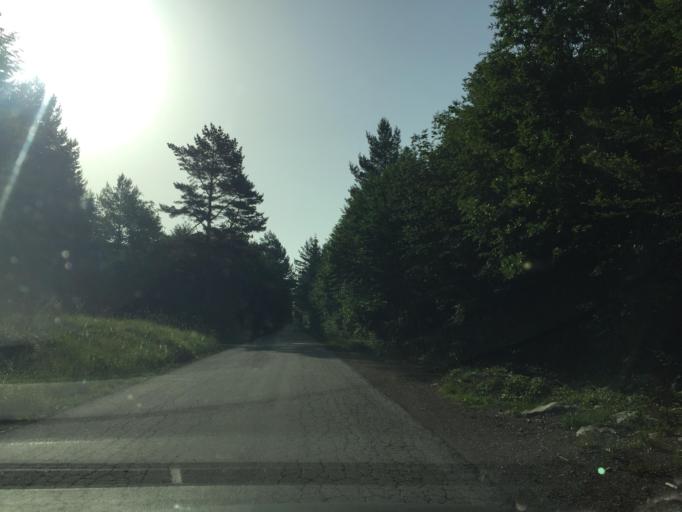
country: HR
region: Istarska
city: Buzet
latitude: 45.4765
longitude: 14.0762
